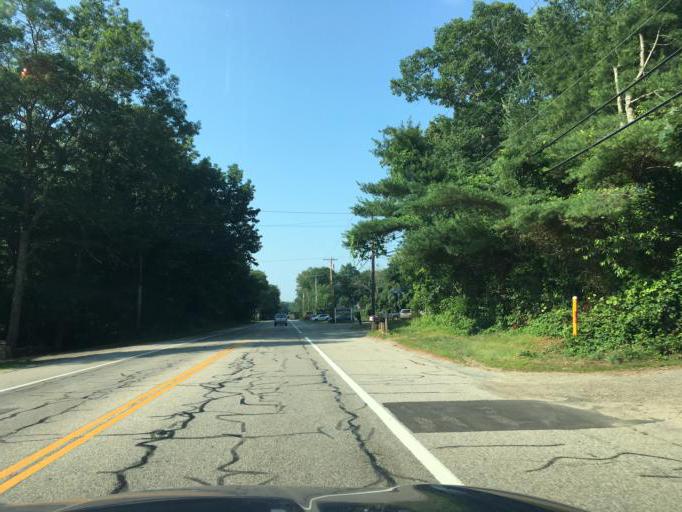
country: US
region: Rhode Island
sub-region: Washington County
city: Kingston
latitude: 41.5198
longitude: -71.5544
